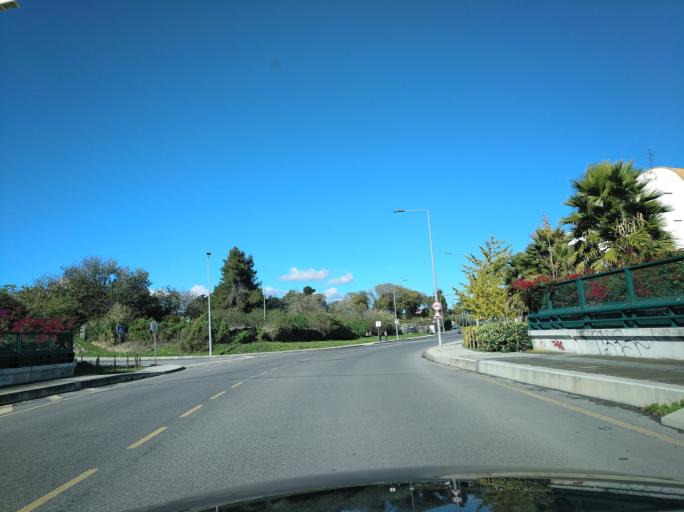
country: PT
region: Lisbon
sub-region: Lisbon
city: Lisbon
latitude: 38.7374
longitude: -9.1128
